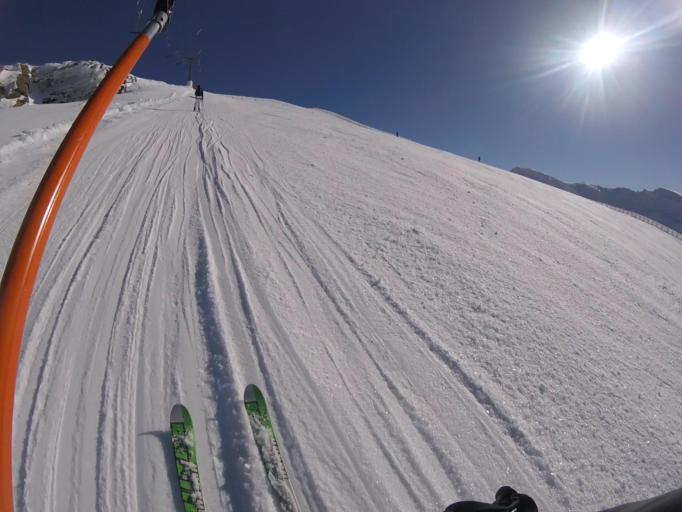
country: ES
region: Andalusia
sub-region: Provincia de Granada
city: Capileira
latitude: 37.0609
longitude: -3.3755
